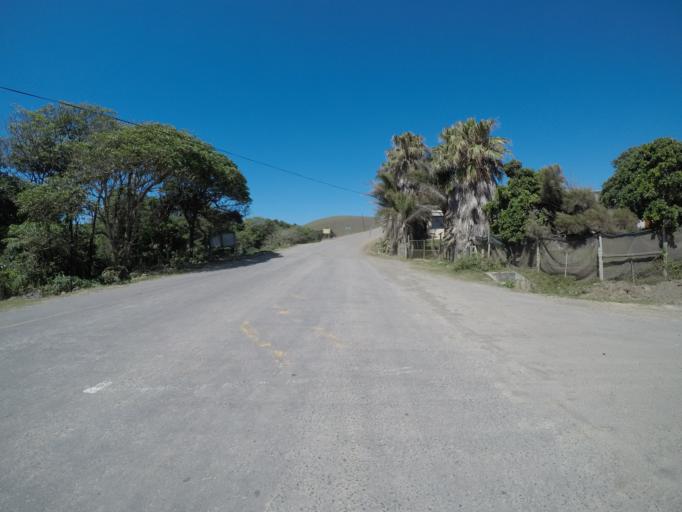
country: ZA
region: Eastern Cape
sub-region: OR Tambo District Municipality
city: Libode
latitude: -31.9860
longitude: 29.1482
